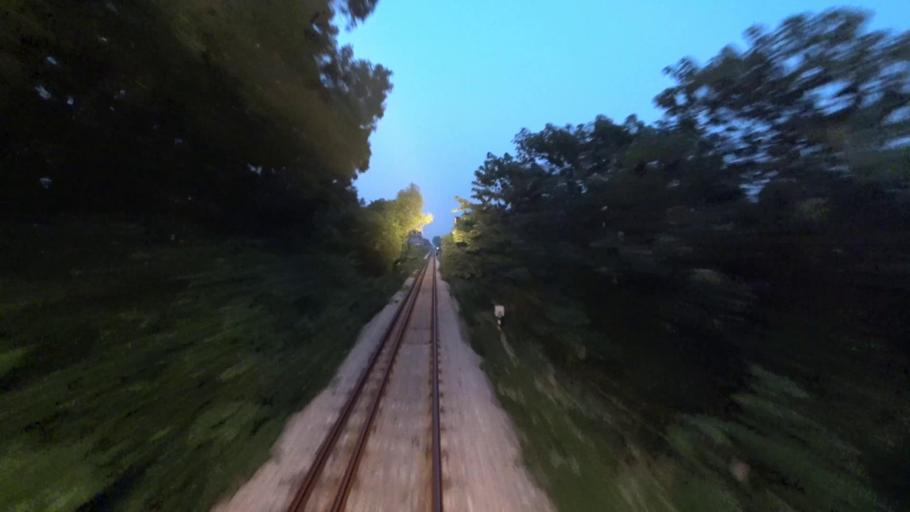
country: VN
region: Ha Noi
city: Soc Son
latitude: 21.2559
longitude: 105.8619
